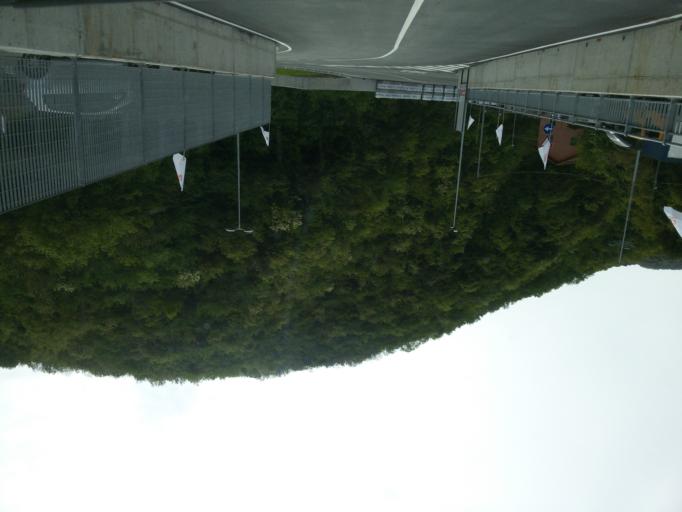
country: IT
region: Liguria
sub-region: Provincia di Genova
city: Piccarello
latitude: 44.4349
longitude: 8.9696
